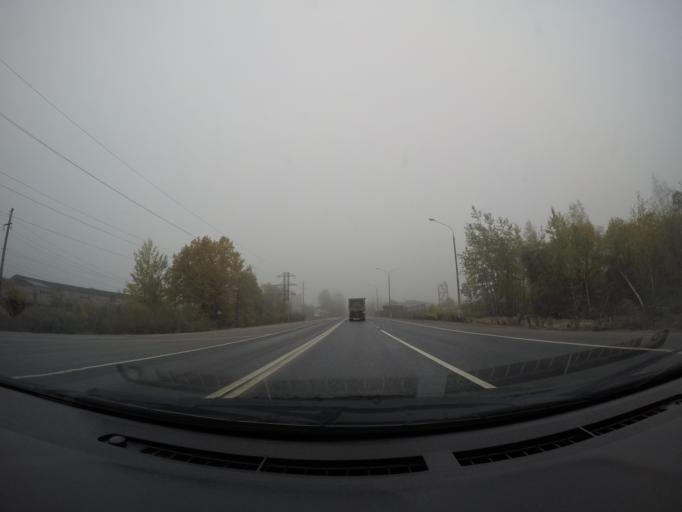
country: RU
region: Moskovskaya
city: Rumyantsevo
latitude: 55.8765
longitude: 36.5595
